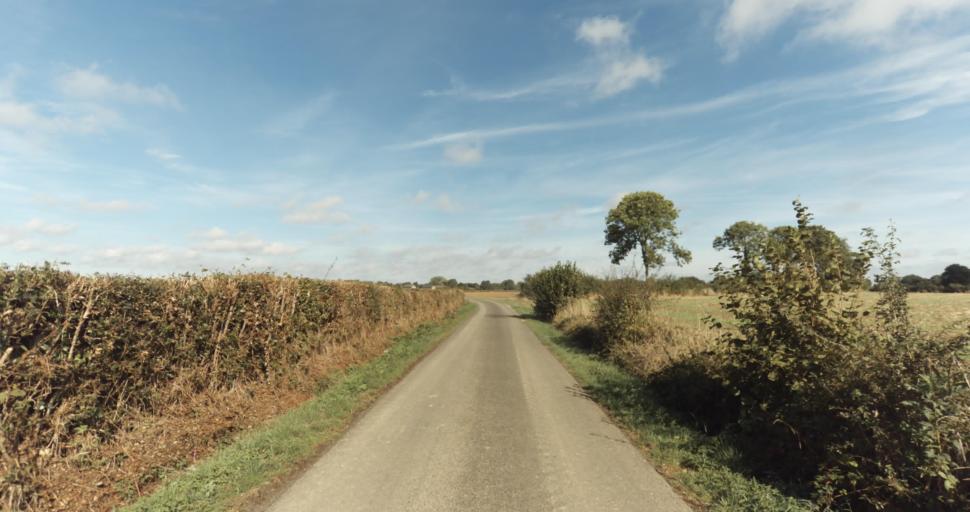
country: FR
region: Lower Normandy
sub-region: Departement du Calvados
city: Orbec
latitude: 48.9287
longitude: 0.3491
